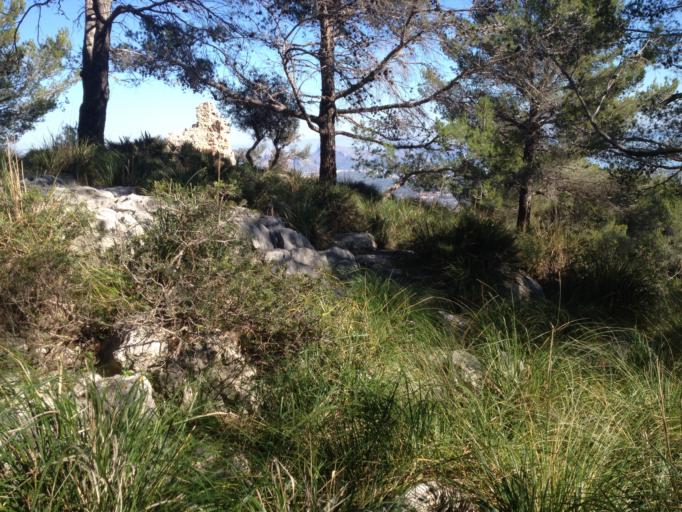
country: ES
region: Balearic Islands
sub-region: Illes Balears
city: Pollenca
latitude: 39.8690
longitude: 3.0238
